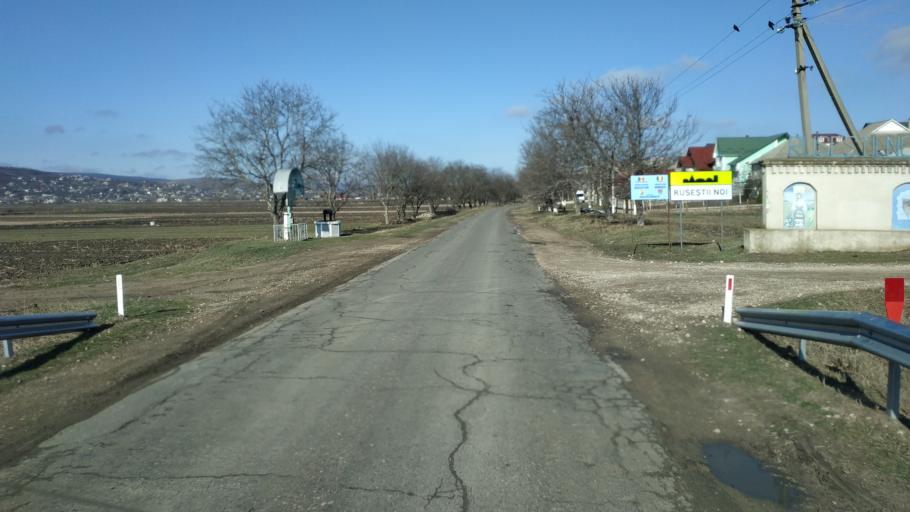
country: MD
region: Laloveni
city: Ialoveni
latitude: 46.9284
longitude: 28.6734
